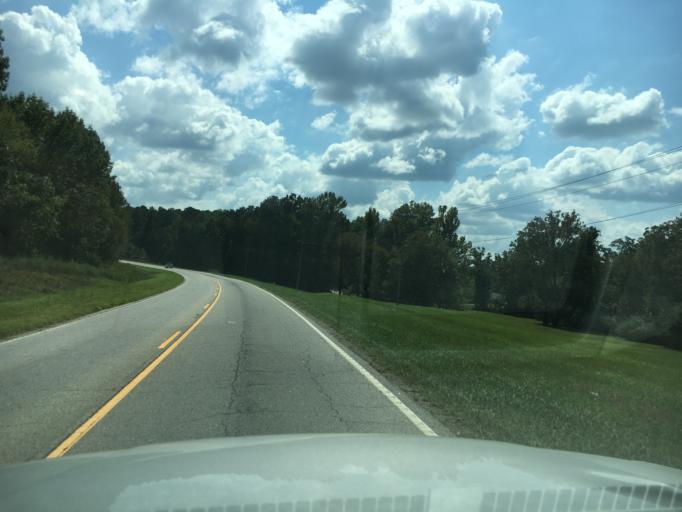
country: US
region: South Carolina
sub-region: Greenwood County
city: Greenwood
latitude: 34.1655
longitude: -82.1832
